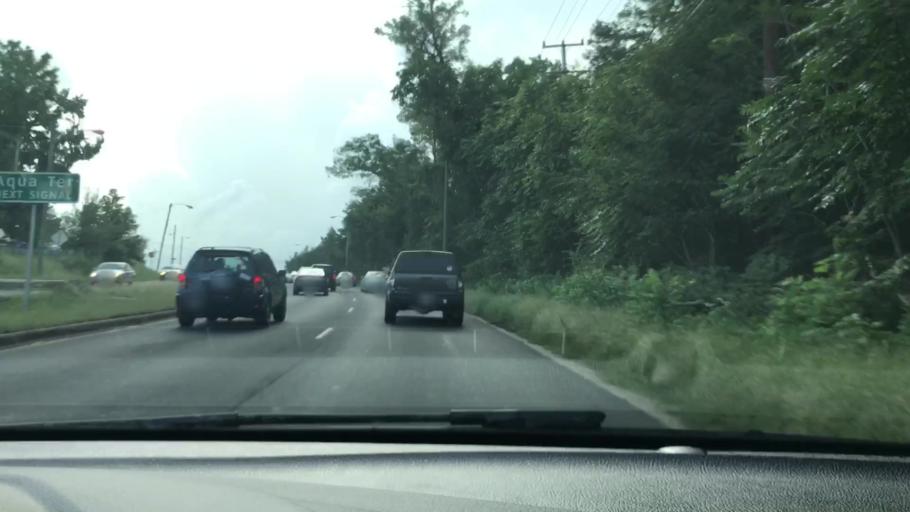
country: US
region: Virginia
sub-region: Fairfax County
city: Lake Barcroft
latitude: 38.8423
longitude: -77.1473
